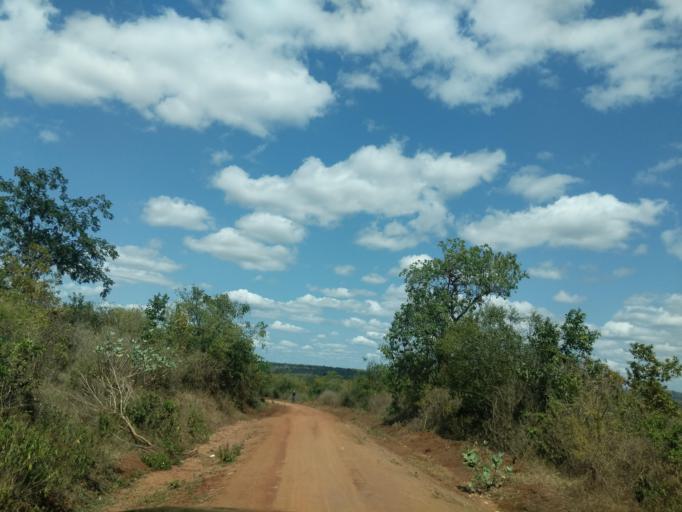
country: TZ
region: Tanga
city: Chanika
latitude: -5.5068
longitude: 38.3665
